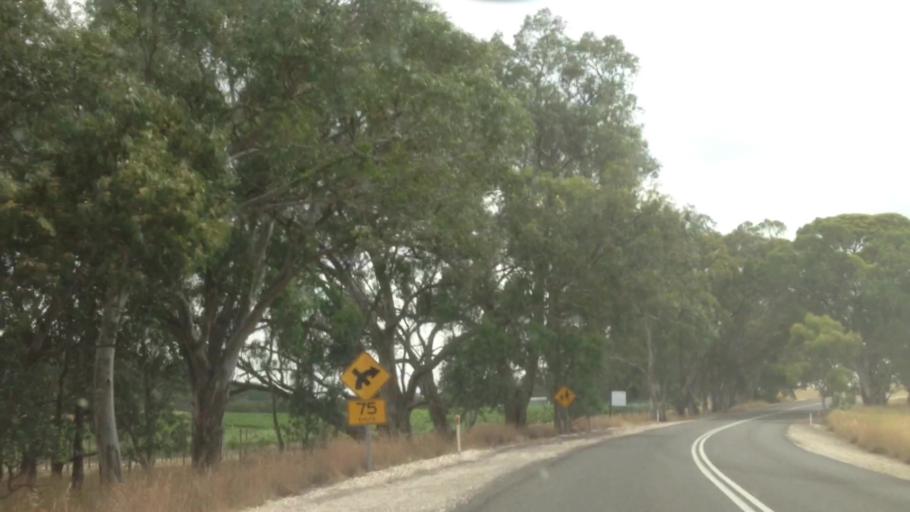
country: AU
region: South Australia
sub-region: Barossa
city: Williamstown
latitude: -34.6874
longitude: 138.9722
